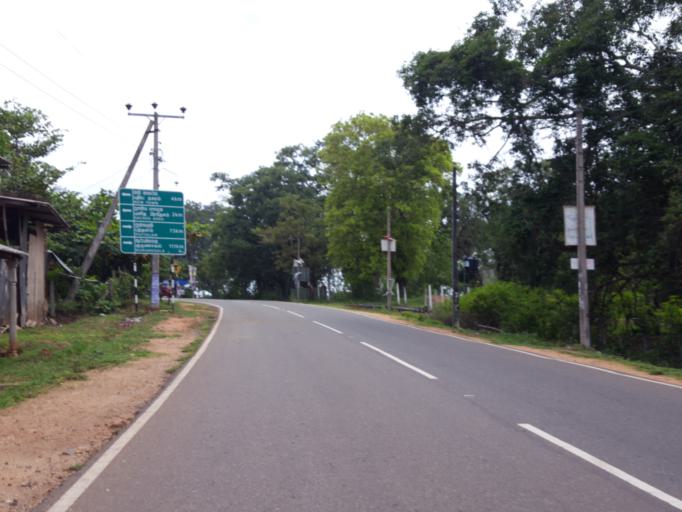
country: LK
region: North Central
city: Anuradhapura
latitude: 8.3416
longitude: 80.3789
